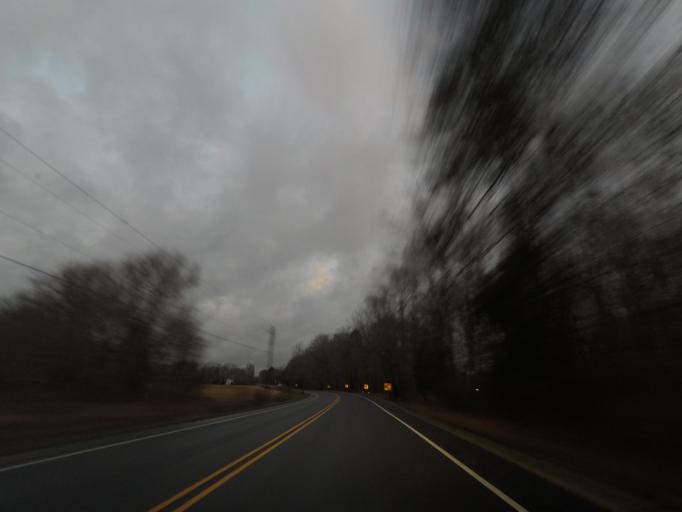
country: US
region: North Carolina
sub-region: Orange County
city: Hillsborough
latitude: 36.1483
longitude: -79.1231
